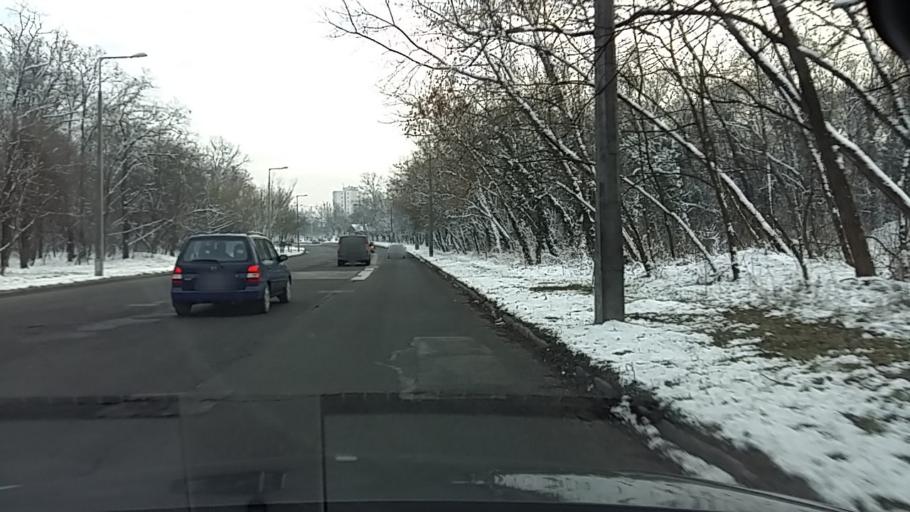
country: HU
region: Budapest
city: Budapest XV. keruelet
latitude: 47.5839
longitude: 19.1042
